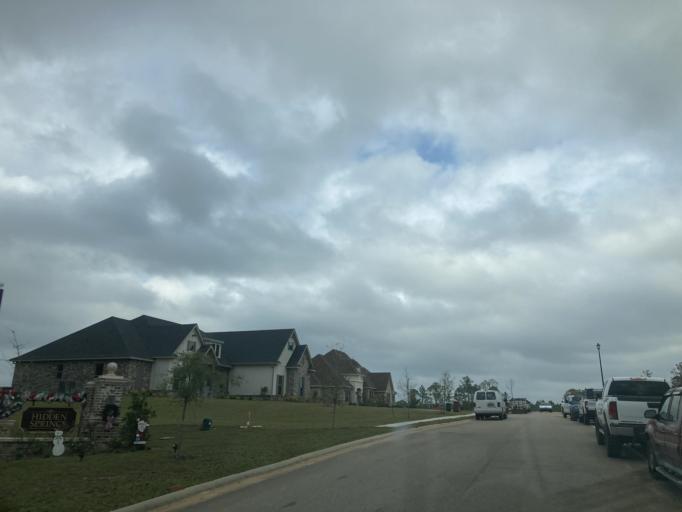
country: US
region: Mississippi
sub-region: Harrison County
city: D'Iberville
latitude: 30.4862
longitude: -88.9975
